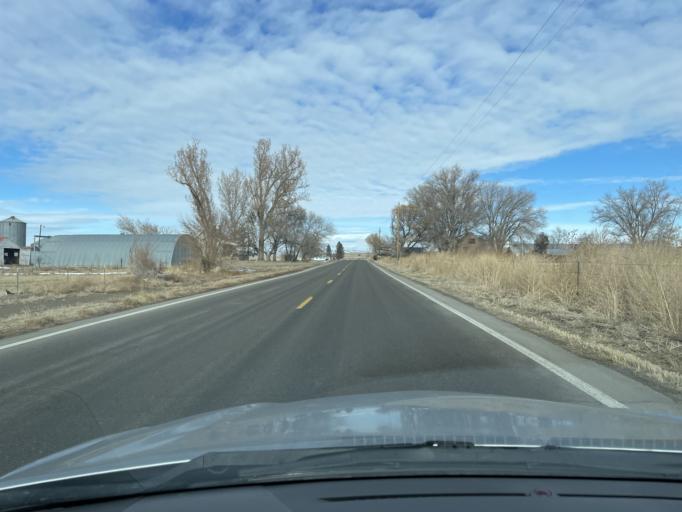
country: US
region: Colorado
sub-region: Mesa County
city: Loma
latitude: 39.2544
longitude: -108.8128
